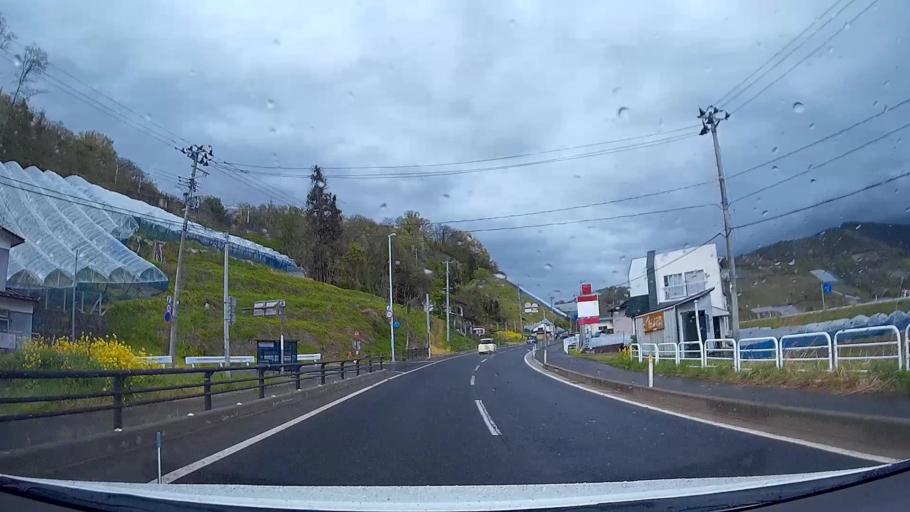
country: JP
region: Yamagata
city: Takahata
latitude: 38.0575
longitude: 140.1728
